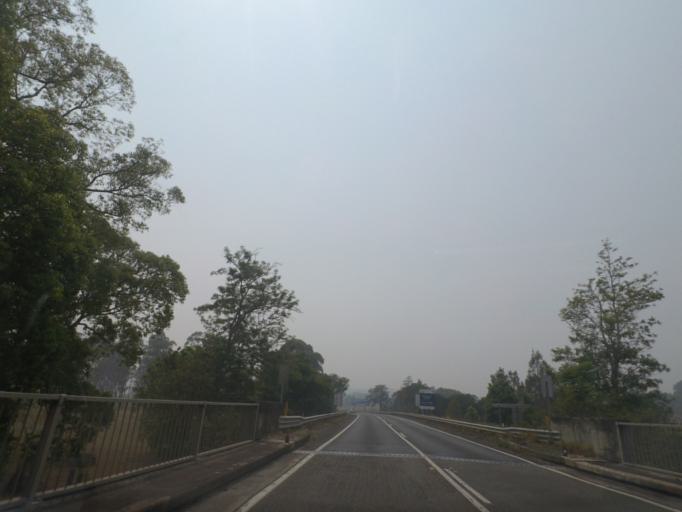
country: AU
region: New South Wales
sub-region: Clarence Valley
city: Maclean
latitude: -29.5669
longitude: 153.1298
